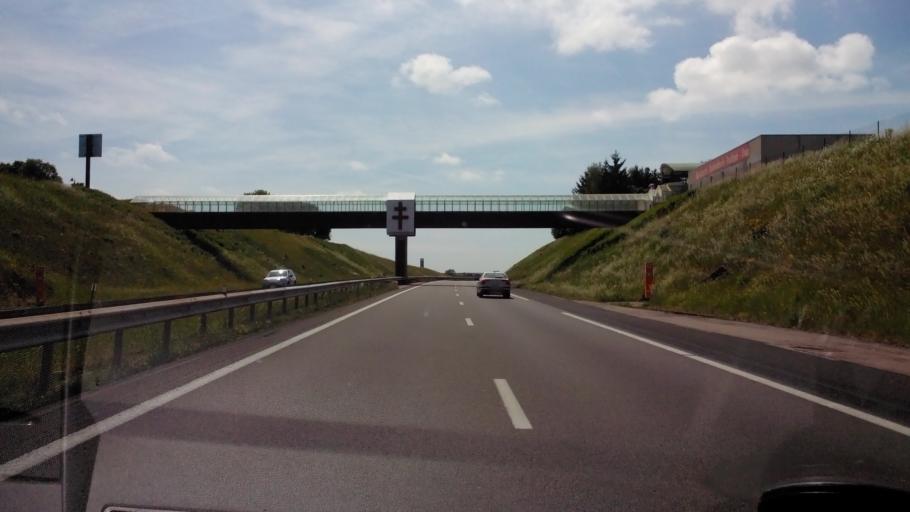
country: FR
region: Lorraine
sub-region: Departement des Vosges
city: Chatenois
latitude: 48.2687
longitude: 5.8615
